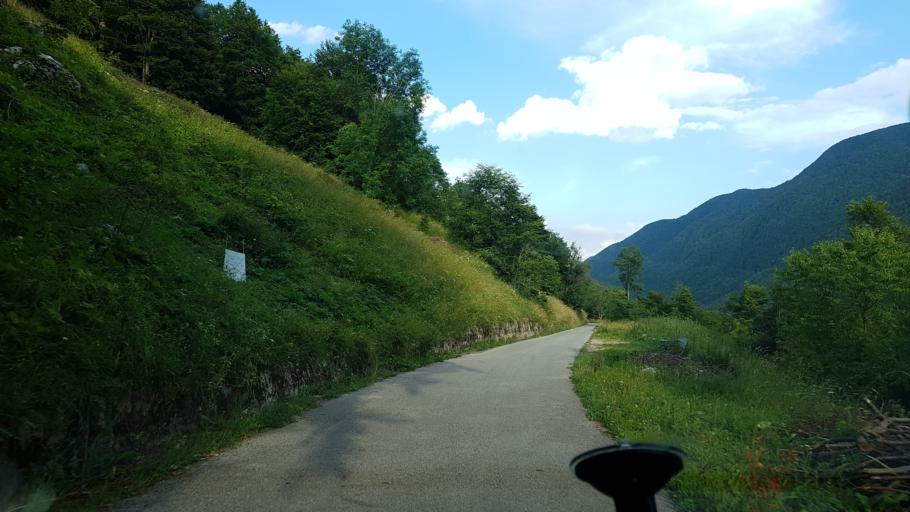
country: IT
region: Friuli Venezia Giulia
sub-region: Provincia di Udine
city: Prato
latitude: 46.3339
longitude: 13.3332
